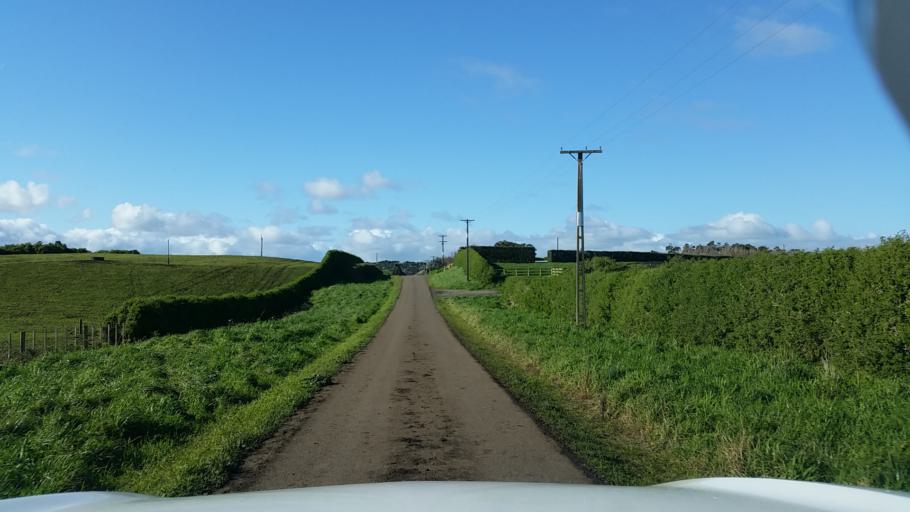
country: NZ
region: Taranaki
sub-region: South Taranaki District
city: Hawera
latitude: -39.6643
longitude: 174.3727
